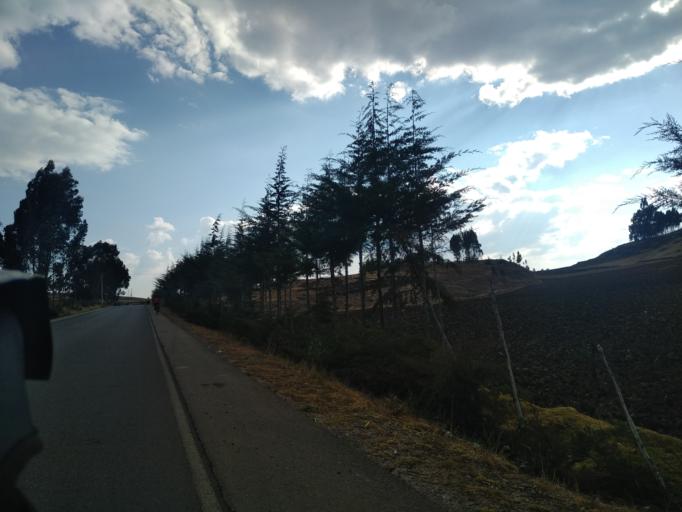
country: PE
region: Cajamarca
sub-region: Provincia de Cajamarca
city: Llacanora
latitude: -7.1448
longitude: -78.3941
